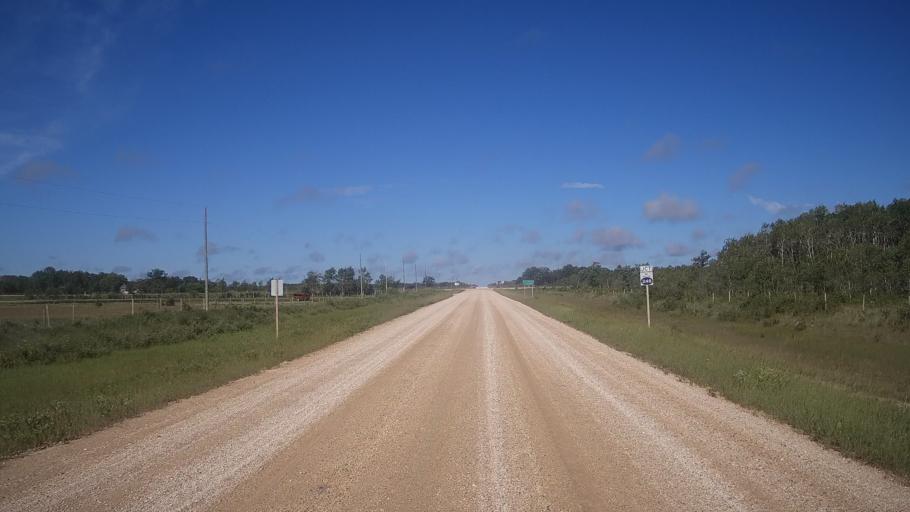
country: CA
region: Manitoba
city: Stonewall
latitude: 50.2411
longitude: -97.7315
